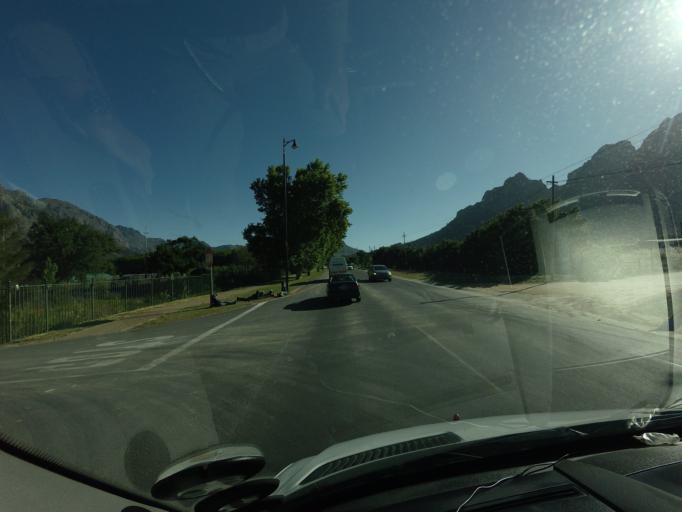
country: ZA
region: Western Cape
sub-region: Cape Winelands District Municipality
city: Stellenbosch
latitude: -33.8846
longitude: 18.9672
